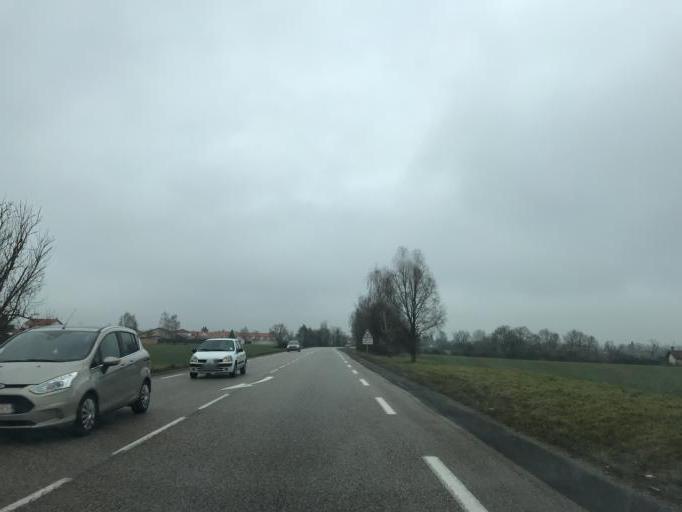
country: FR
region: Rhone-Alpes
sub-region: Departement de l'Ain
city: Saint-Denis-les-Bourg
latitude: 46.1982
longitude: 5.1982
